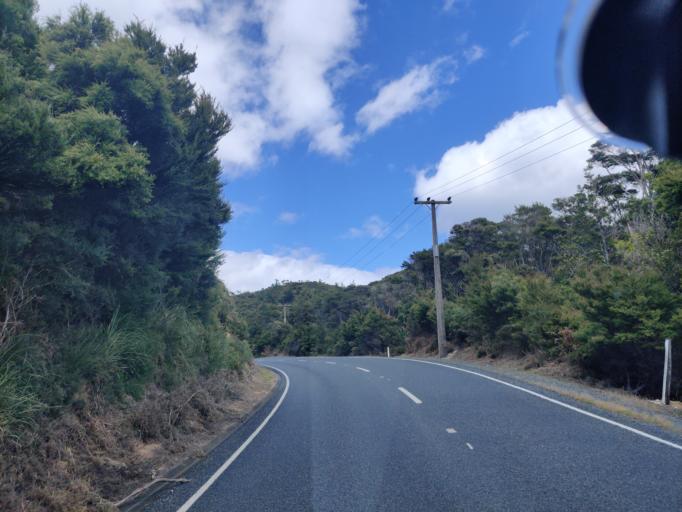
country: NZ
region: Northland
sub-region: Far North District
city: Paihia
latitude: -35.2599
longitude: 174.2234
